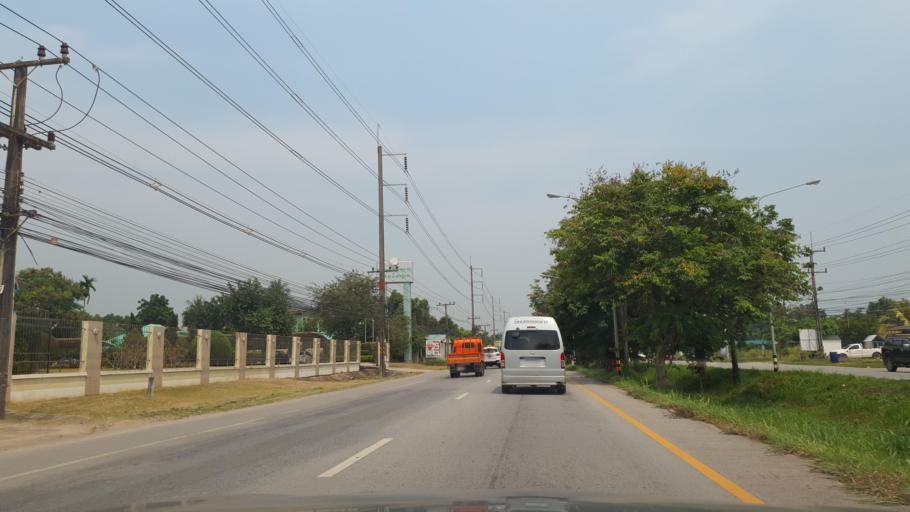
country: TH
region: Rayong
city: Rayong
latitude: 12.6421
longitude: 101.3578
